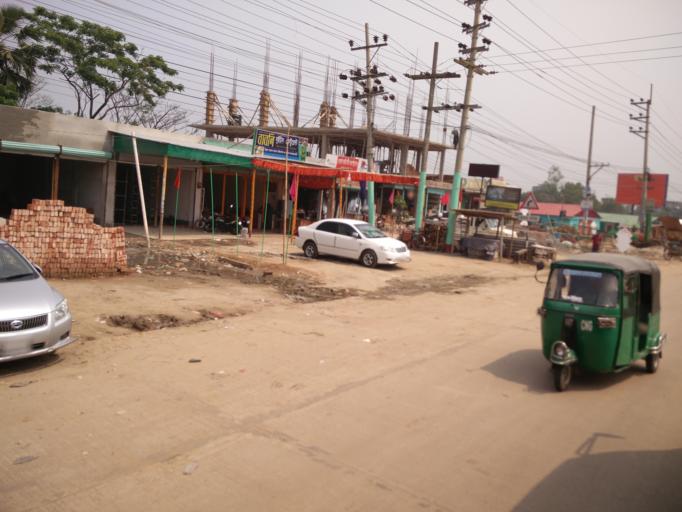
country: BD
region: Dhaka
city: Gafargaon
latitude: 24.4041
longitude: 90.3863
